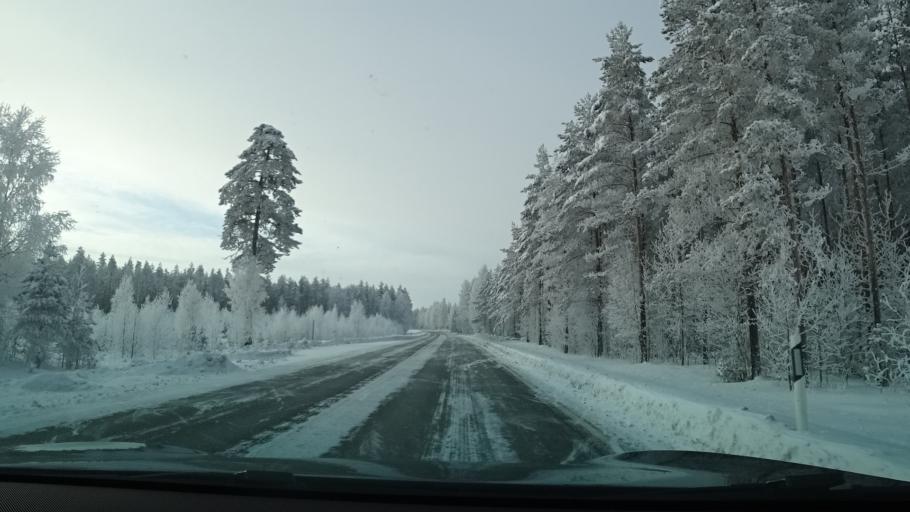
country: FI
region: South Karelia
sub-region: Imatra
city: Saari
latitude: 61.7771
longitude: 29.6967
